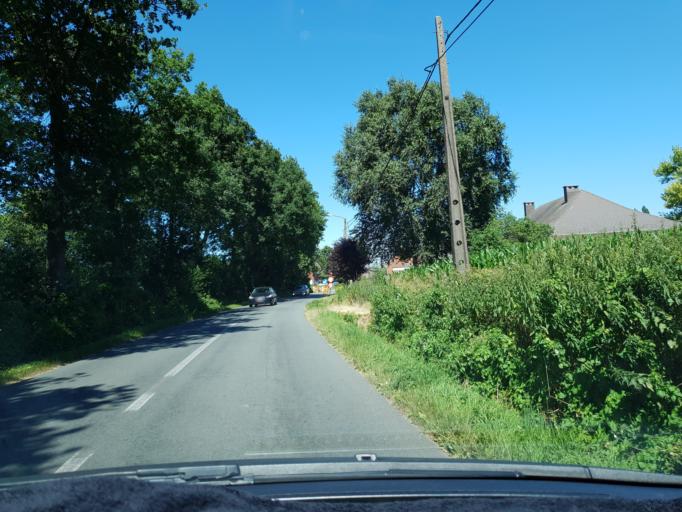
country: BE
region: Flanders
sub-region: Provincie Antwerpen
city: Geel
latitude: 51.1593
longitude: 4.9409
